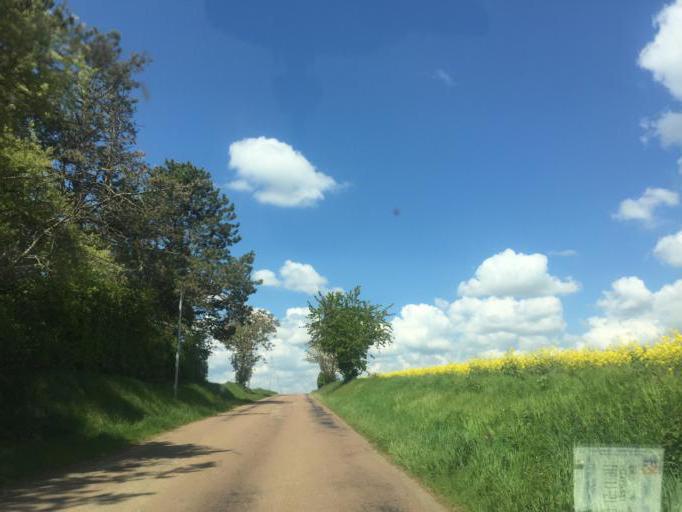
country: FR
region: Bourgogne
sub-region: Departement de l'Yonne
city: Fontenailles
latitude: 47.5001
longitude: 3.3627
